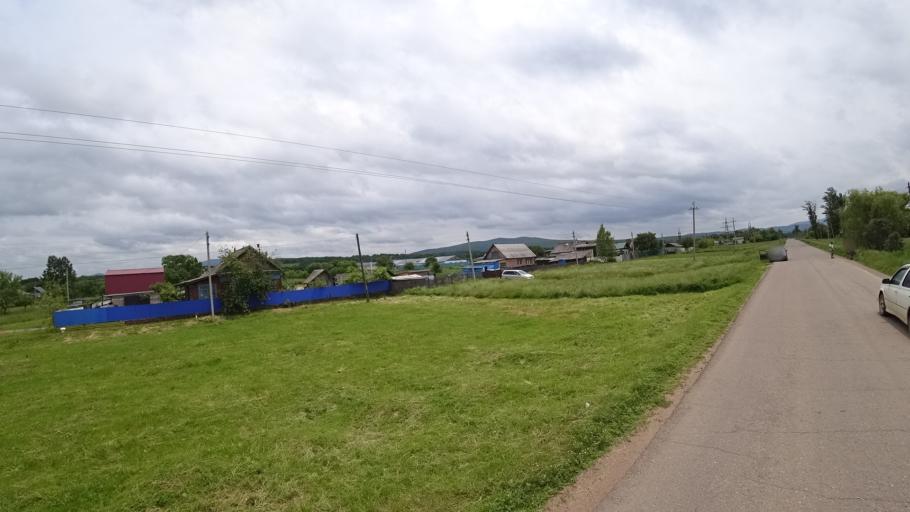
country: RU
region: Primorskiy
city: Novosysoyevka
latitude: 44.2369
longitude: 133.3696
